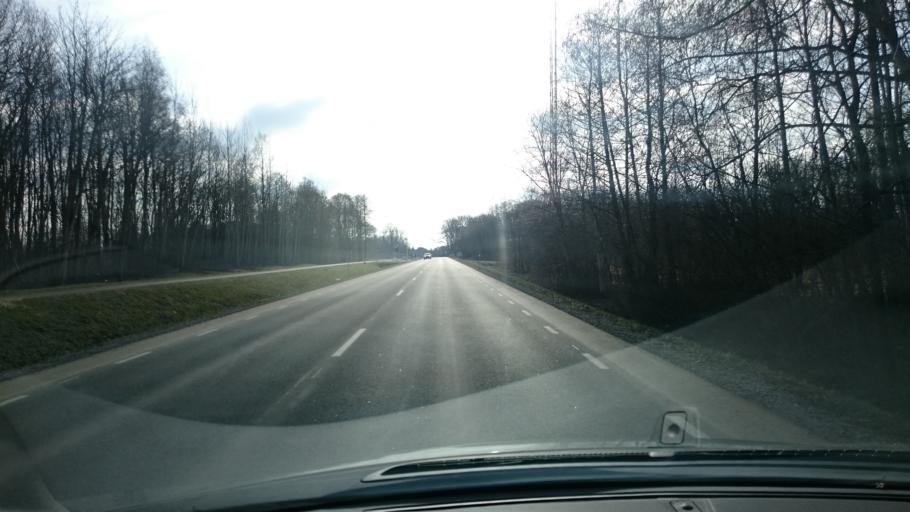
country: EE
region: Harju
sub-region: Paldiski linn
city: Paldiski
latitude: 59.3821
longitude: 24.2360
